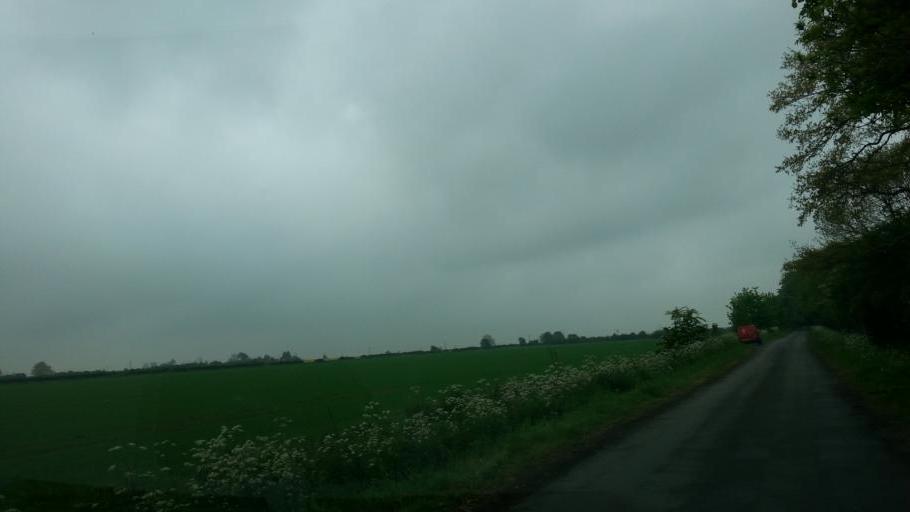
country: GB
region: England
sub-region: Lincolnshire
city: Long Bennington
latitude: 53.0432
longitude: -0.7631
